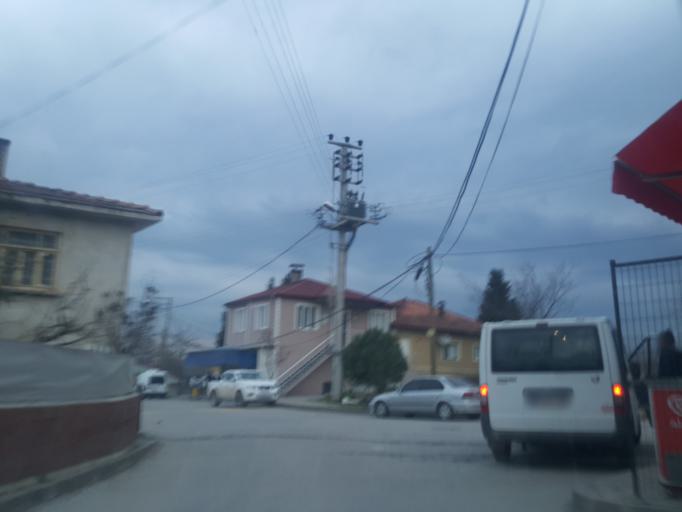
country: TR
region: Kocaeli
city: Tavsanli
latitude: 40.8467
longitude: 29.5550
